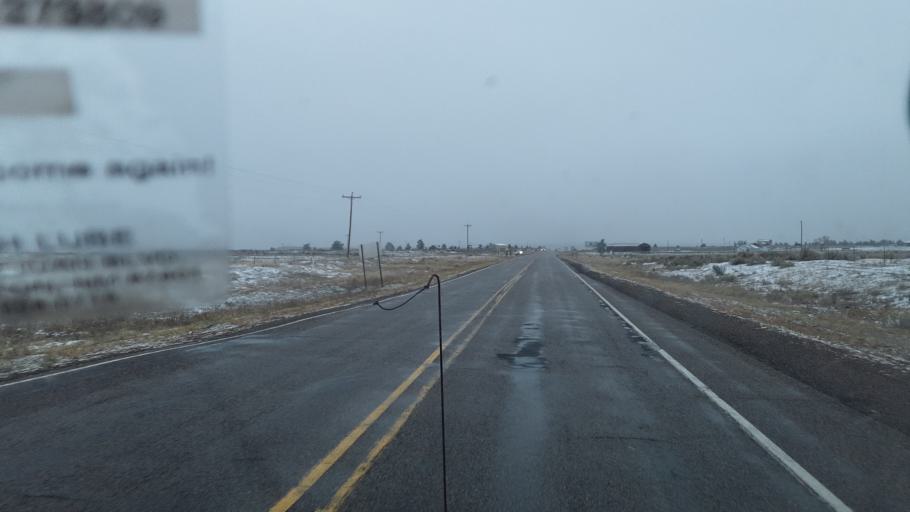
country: US
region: New Mexico
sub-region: Rio Arriba County
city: Tierra Amarilla
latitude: 36.7183
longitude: -106.5626
